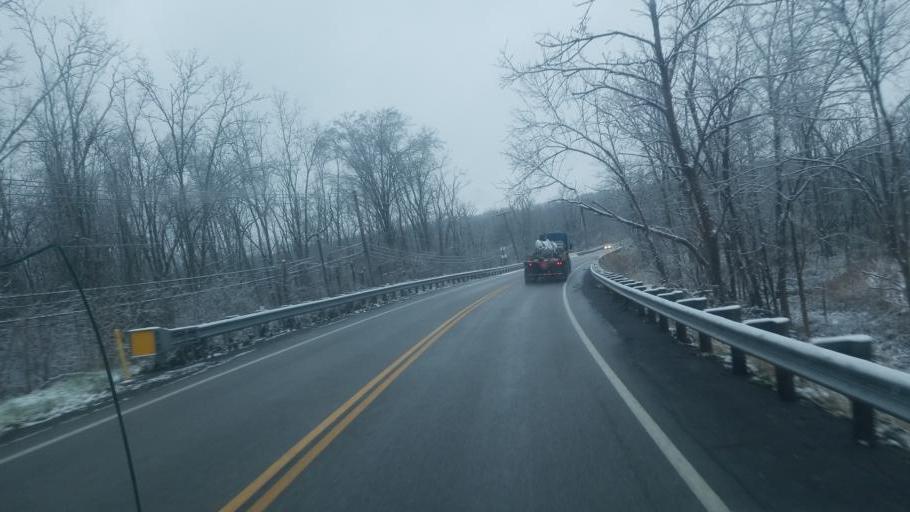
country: US
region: Ohio
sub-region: Geauga County
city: Burton
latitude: 41.4591
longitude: -81.1378
